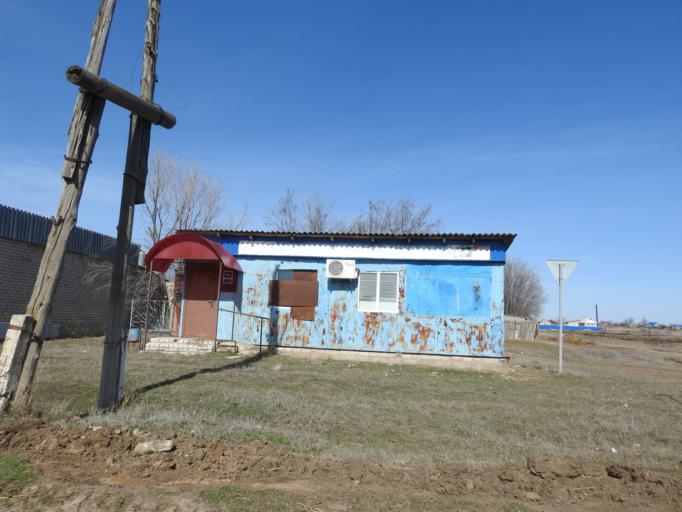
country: RU
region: Volgograd
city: Staraya Poltavka
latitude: 50.4296
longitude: 46.3927
